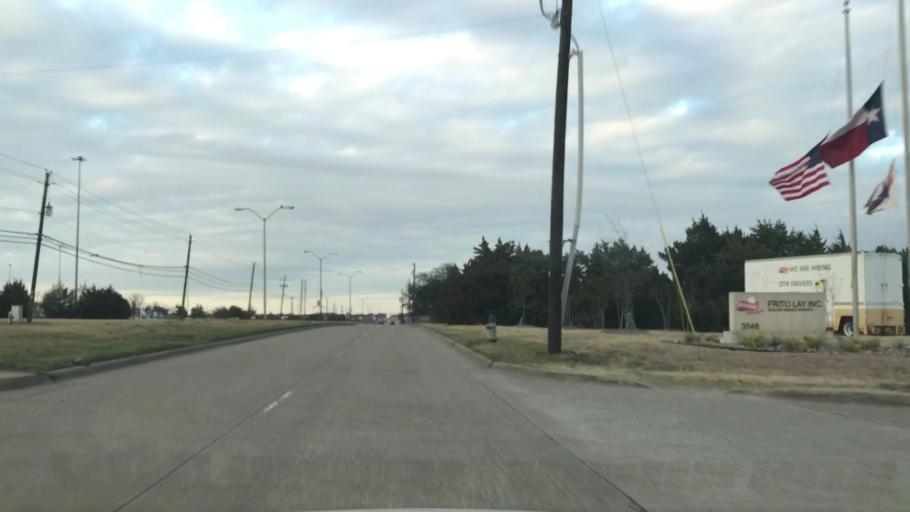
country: US
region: Texas
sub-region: Dallas County
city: Cockrell Hill
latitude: 32.7007
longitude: -96.9086
